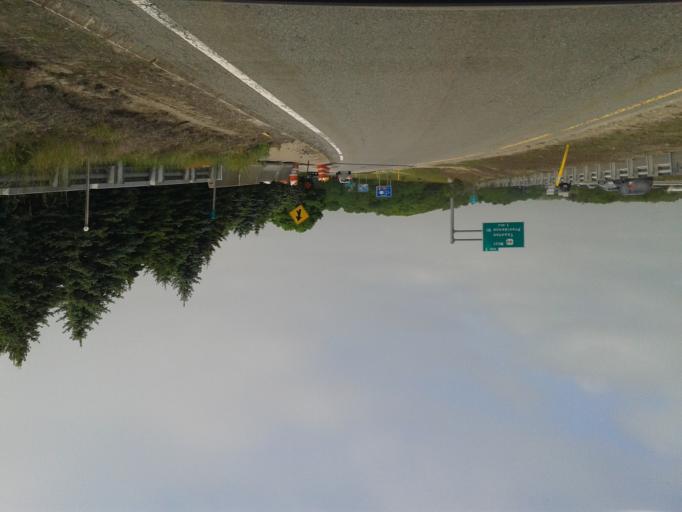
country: US
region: Massachusetts
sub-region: Plymouth County
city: Plymouth
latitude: 41.9520
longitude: -70.6799
